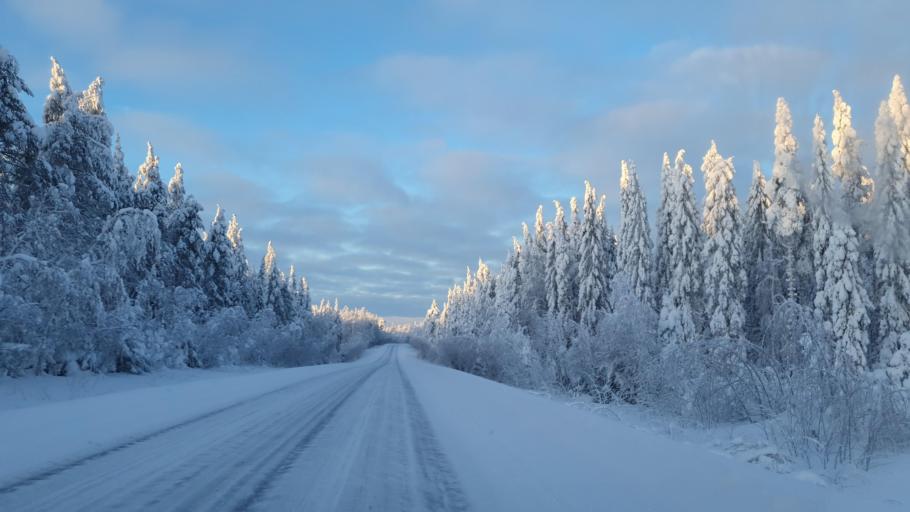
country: FI
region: Kainuu
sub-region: Kajaani
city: Vuokatti
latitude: 64.2742
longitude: 28.2336
